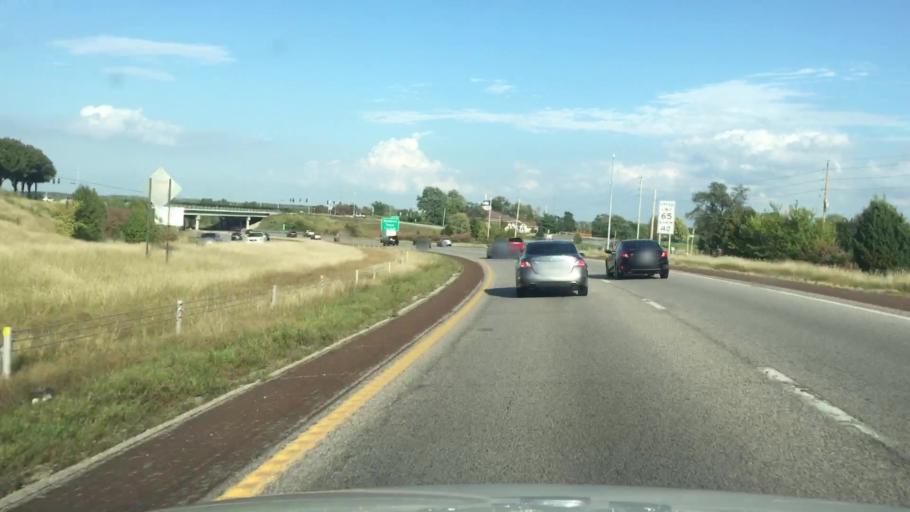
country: US
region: Missouri
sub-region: Jackson County
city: Lees Summit
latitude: 38.9449
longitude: -94.3676
